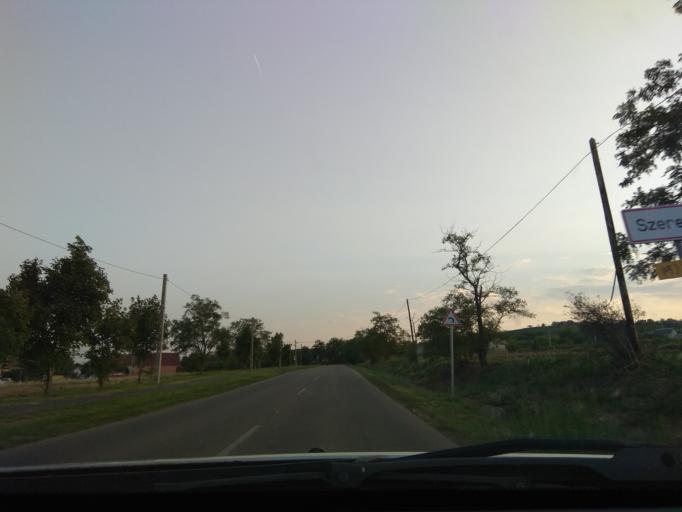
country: HU
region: Borsod-Abauj-Zemplen
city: Szerencs
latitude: 48.1769
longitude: 21.2038
